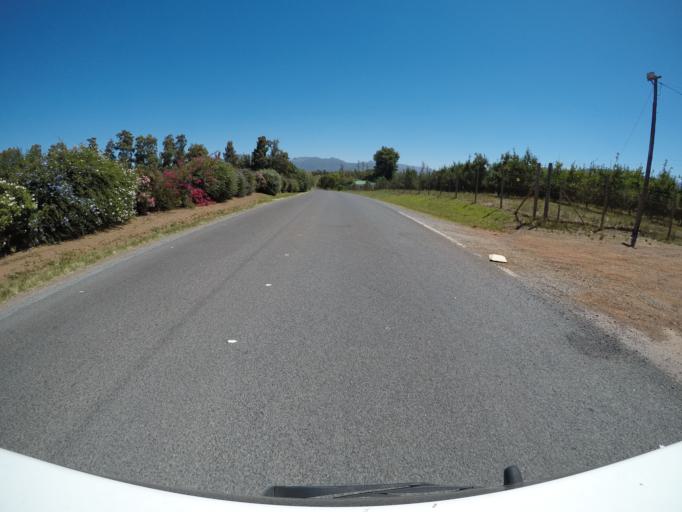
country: ZA
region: Western Cape
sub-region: Overberg District Municipality
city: Grabouw
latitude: -34.1886
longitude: 19.0399
